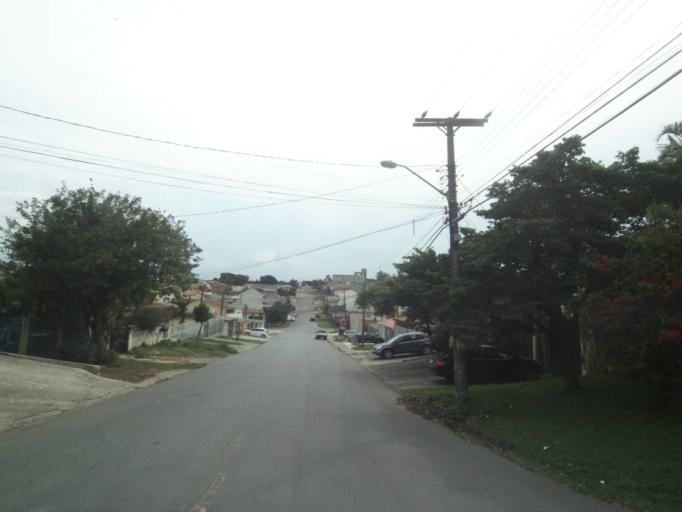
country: BR
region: Parana
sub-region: Pinhais
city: Pinhais
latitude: -25.4011
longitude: -49.2091
